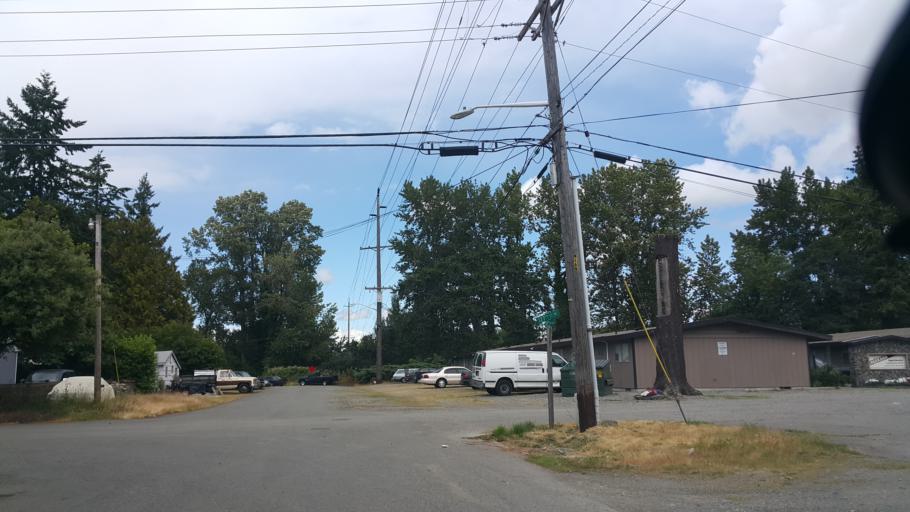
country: US
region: Washington
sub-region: Pierce County
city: McChord Air Force Base
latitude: 47.1421
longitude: -122.4993
